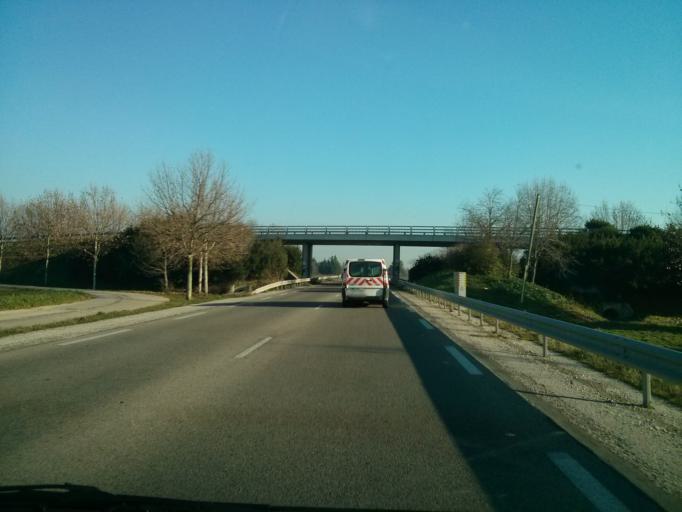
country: FR
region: Languedoc-Roussillon
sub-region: Departement du Gard
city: Uchaud
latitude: 43.7519
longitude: 4.2713
